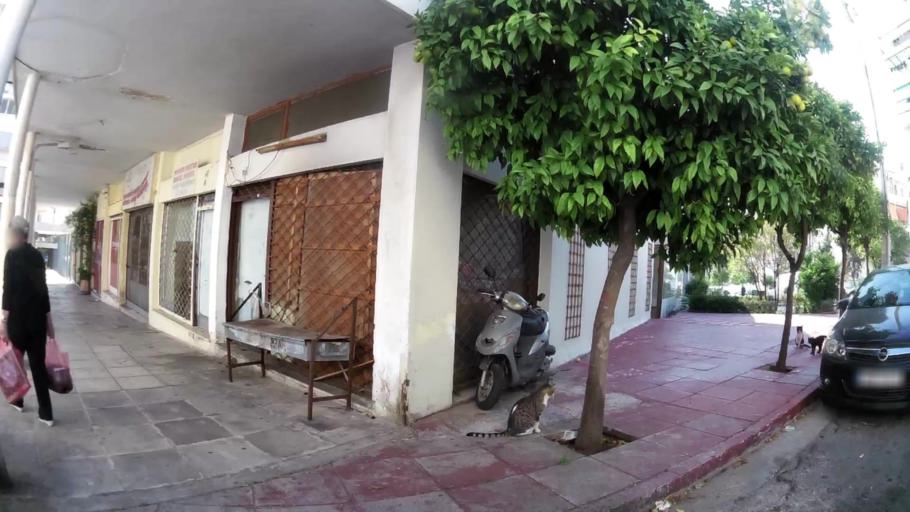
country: GR
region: Attica
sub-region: Nomos Piraios
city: Drapetsona
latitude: 37.9483
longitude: 23.6297
